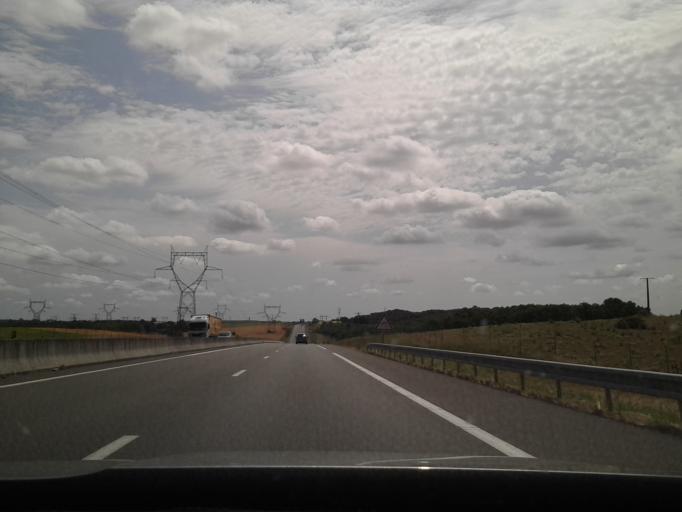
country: FR
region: Centre
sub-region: Departement d'Indre-et-Loire
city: Cerelles
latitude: 47.4901
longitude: 0.6668
